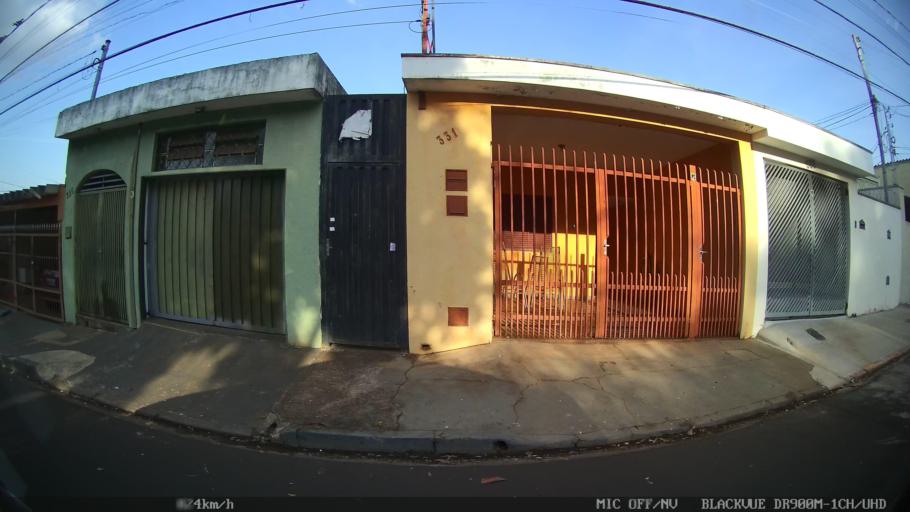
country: BR
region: Sao Paulo
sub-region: Ribeirao Preto
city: Ribeirao Preto
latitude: -21.1693
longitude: -47.8319
